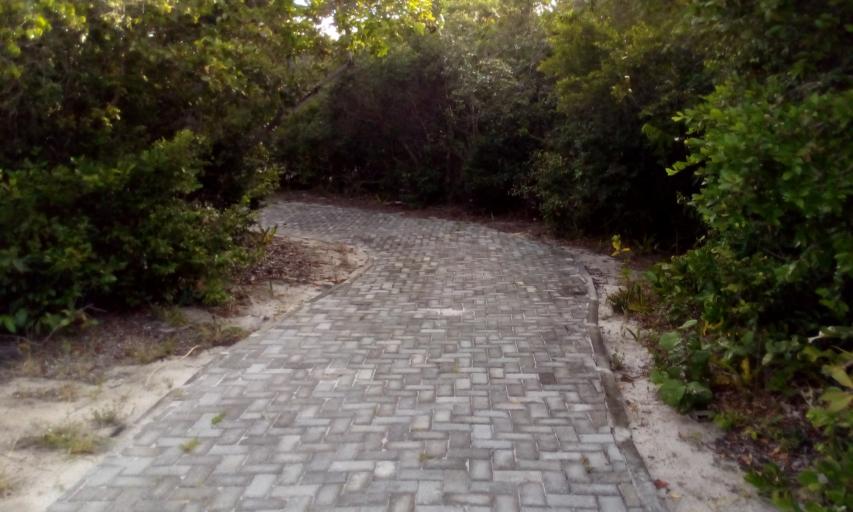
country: BR
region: Bahia
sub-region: Mata De Sao Joao
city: Mata de Sao Joao
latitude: -12.5686
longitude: -38.0034
